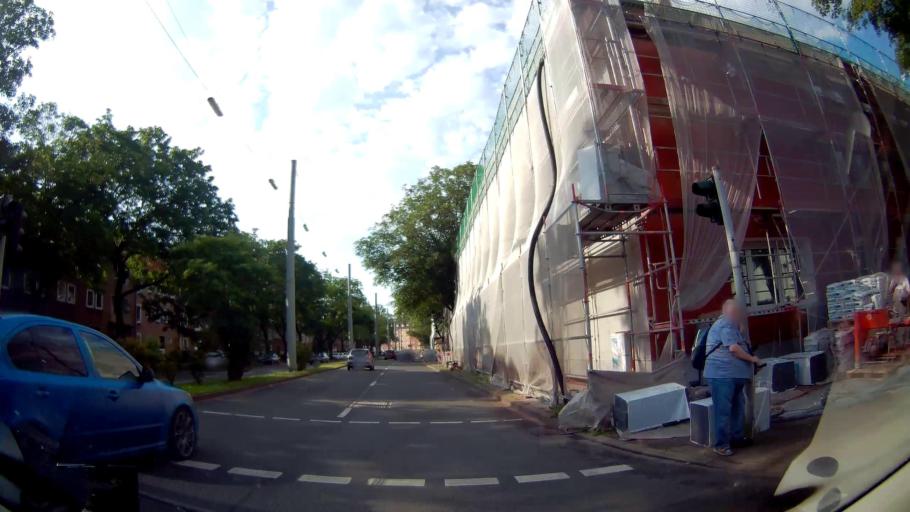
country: DE
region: North Rhine-Westphalia
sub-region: Regierungsbezirk Arnsberg
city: Herne
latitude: 51.5323
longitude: 7.2194
